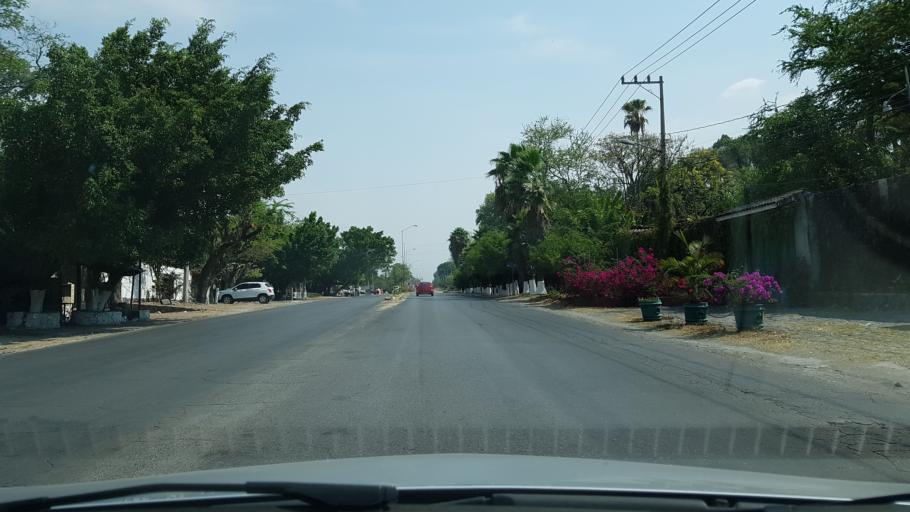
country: MX
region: Morelos
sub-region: Xochitepec
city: Chiconcuac
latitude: 18.7838
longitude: -99.2062
